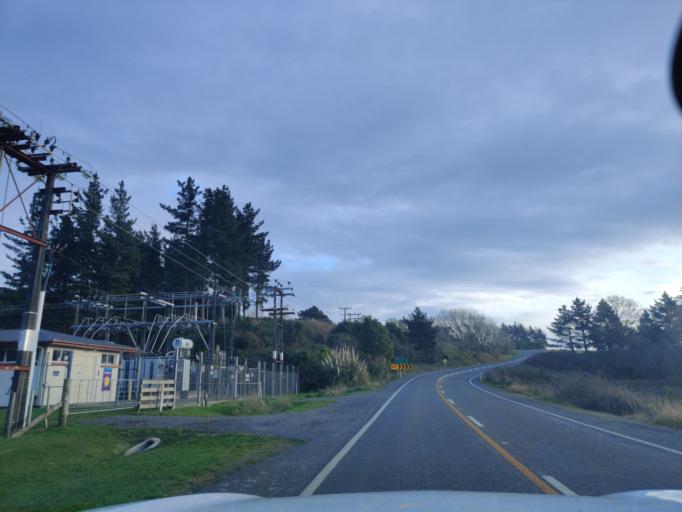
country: NZ
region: Manawatu-Wanganui
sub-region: Palmerston North City
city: Palmerston North
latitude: -40.3940
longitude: 175.6324
